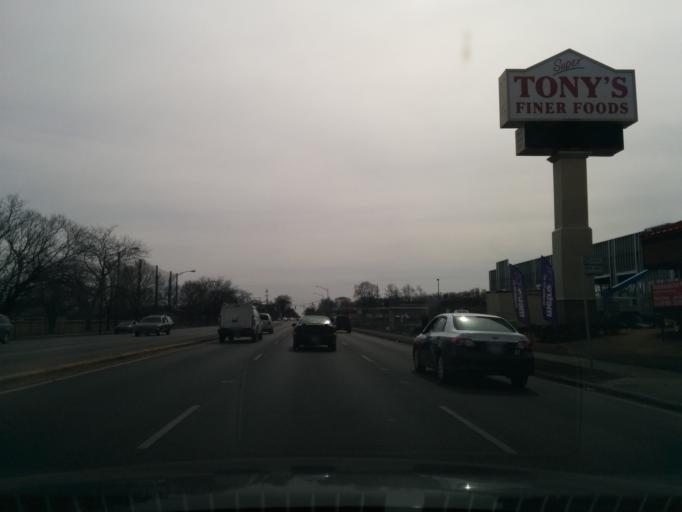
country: US
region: Illinois
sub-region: Cook County
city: Berwyn
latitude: 41.8459
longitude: -87.8036
